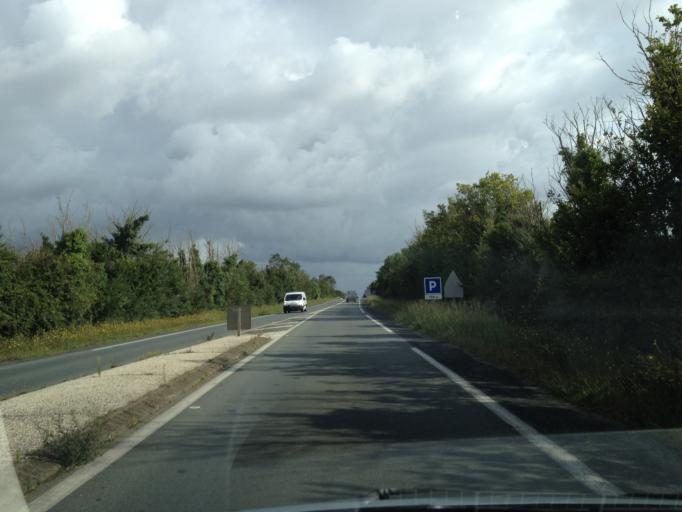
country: FR
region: Poitou-Charentes
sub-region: Departement de la Charente-Maritime
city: Sainte-Soulle
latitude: 46.2202
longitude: -1.0228
